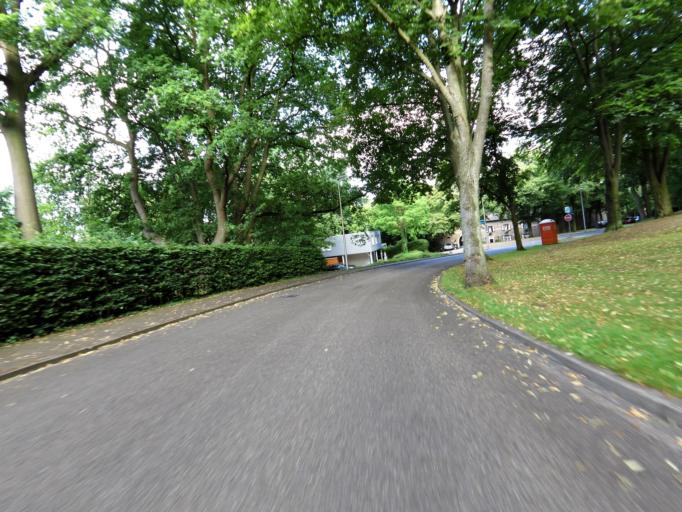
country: NL
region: Limburg
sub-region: Gemeente Heerlen
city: Heerlen
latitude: 50.8822
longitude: 5.9940
